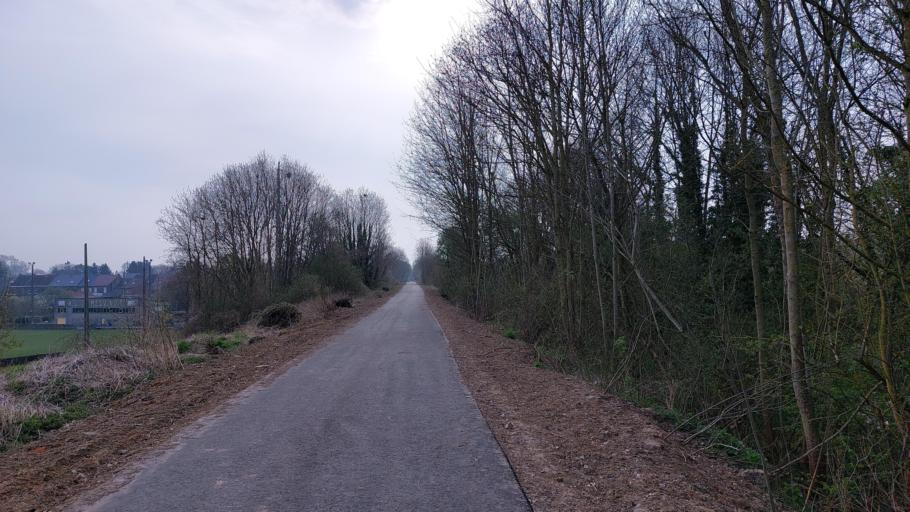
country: BE
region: Wallonia
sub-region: Province du Hainaut
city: Chasse Royale
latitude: 50.4250
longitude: 3.9528
